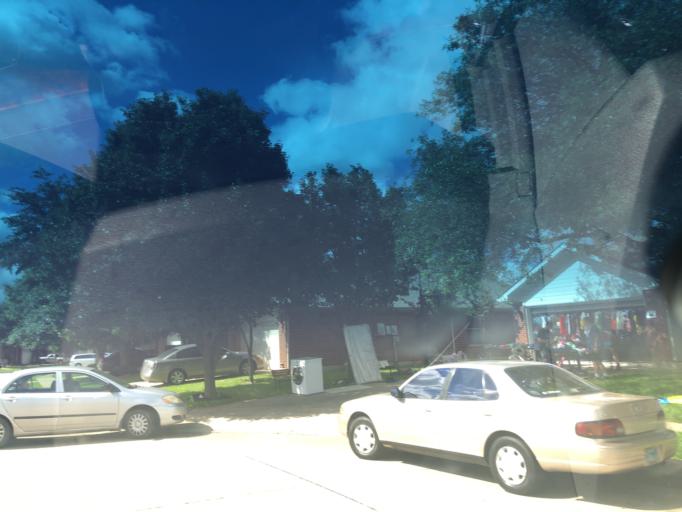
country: US
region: Texas
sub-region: Dallas County
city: Grand Prairie
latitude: 32.6979
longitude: -97.0310
